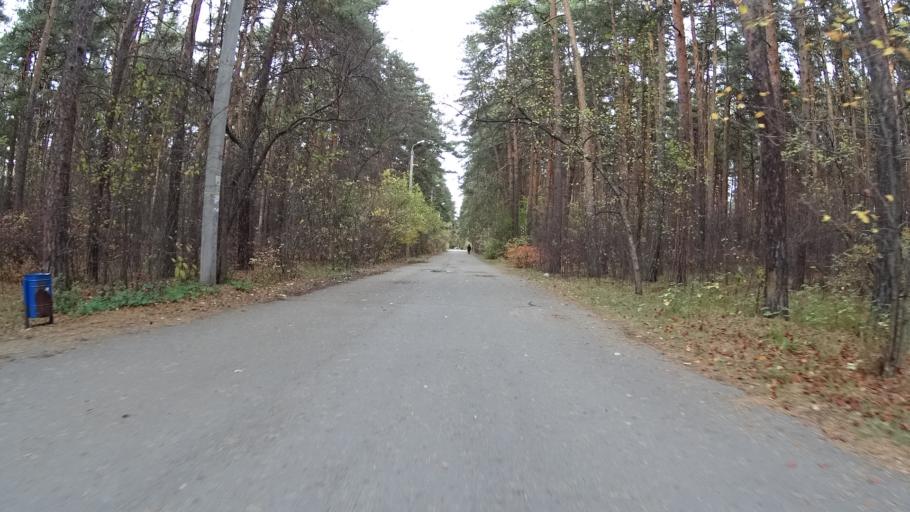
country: RU
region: Chelyabinsk
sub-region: Gorod Chelyabinsk
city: Chelyabinsk
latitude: 55.1525
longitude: 61.3582
